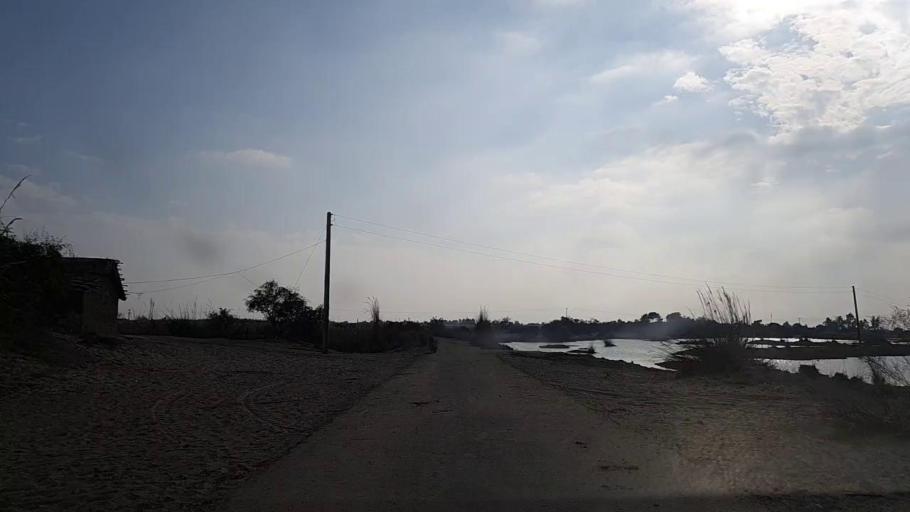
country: PK
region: Sindh
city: Sanghar
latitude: 26.2077
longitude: 69.0217
